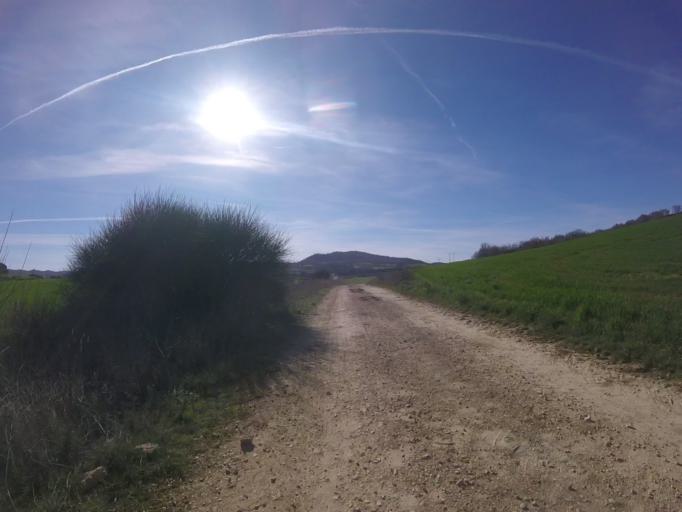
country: ES
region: Navarre
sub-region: Provincia de Navarra
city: Yerri
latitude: 42.6751
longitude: -1.9575
